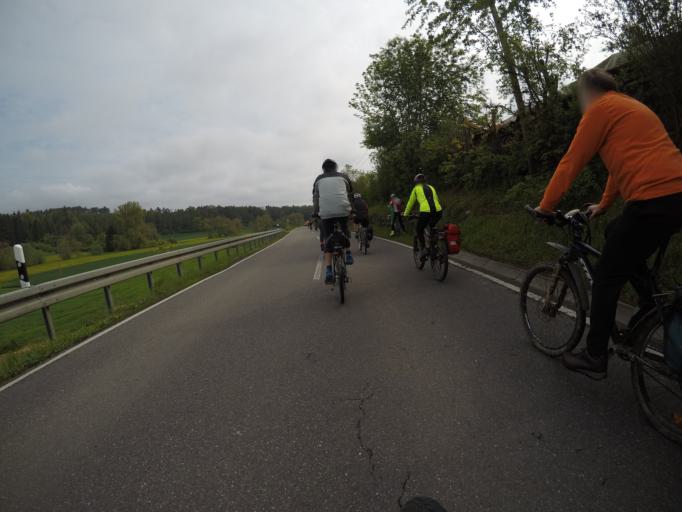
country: DE
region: Baden-Wuerttemberg
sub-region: Regierungsbezirk Stuttgart
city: Weil der Stadt
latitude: 48.7627
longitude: 8.8812
